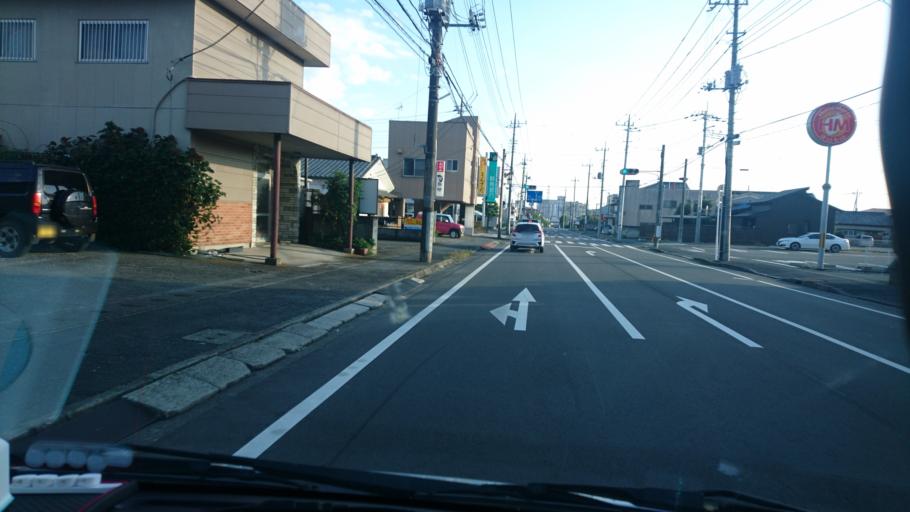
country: JP
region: Gunma
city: Omamacho-omama
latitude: 36.4306
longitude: 139.2771
